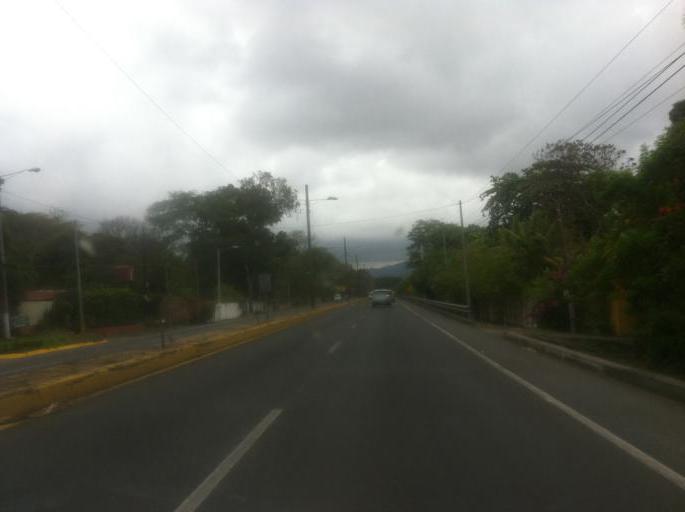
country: NI
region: Masaya
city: Ticuantepe
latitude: 12.0252
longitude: -86.1706
